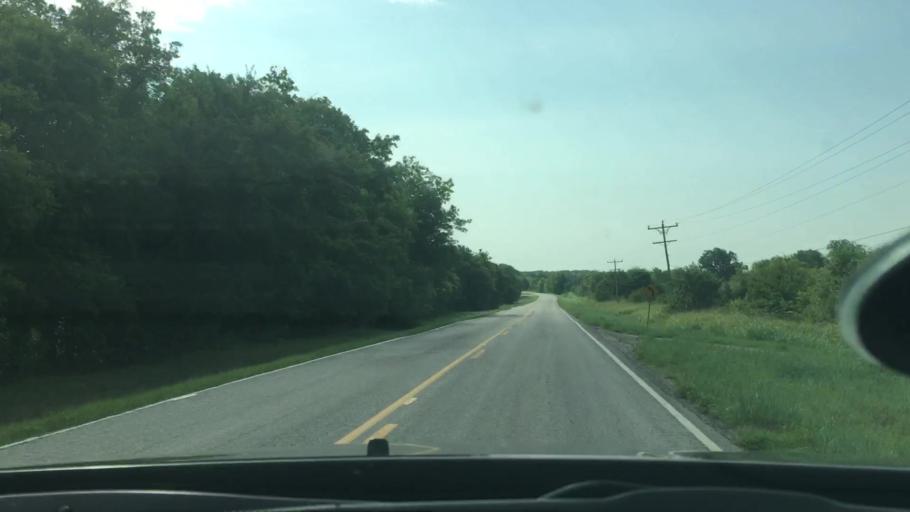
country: US
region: Oklahoma
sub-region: Johnston County
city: Tishomingo
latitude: 34.1473
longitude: -96.5519
